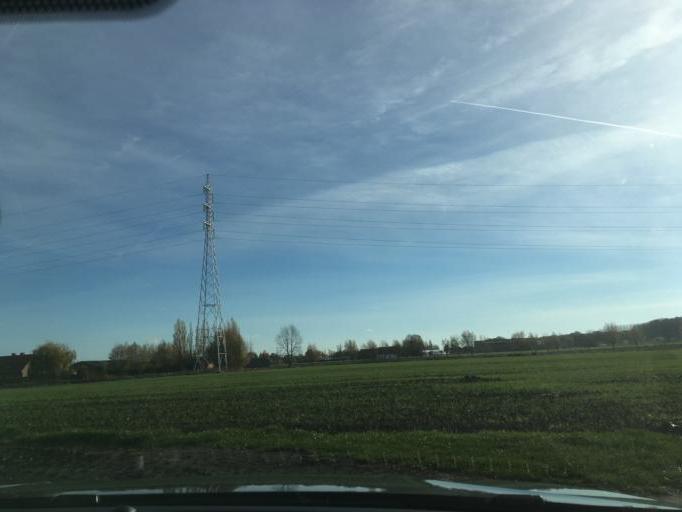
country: BE
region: Flanders
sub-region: Provincie West-Vlaanderen
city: Pittem
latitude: 50.9741
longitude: 3.2371
